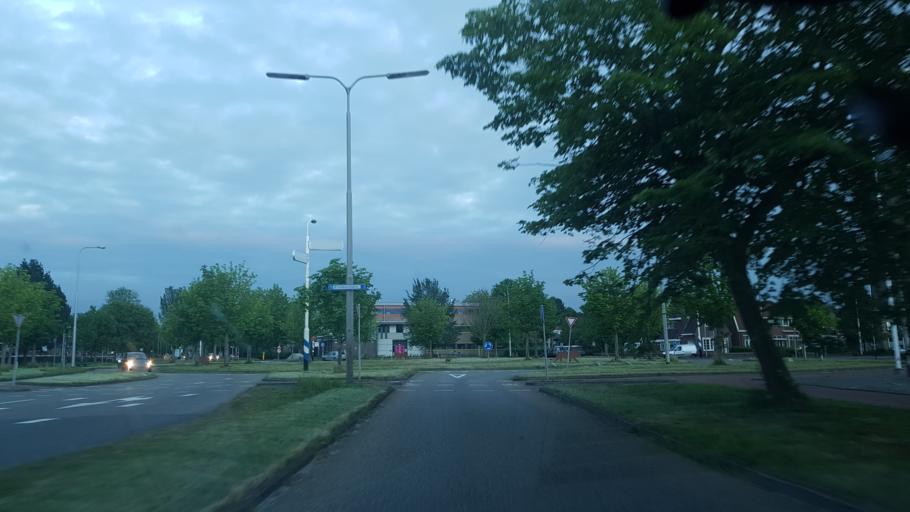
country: NL
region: Friesland
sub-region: Gemeente Leeuwarden
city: Leeuwarden
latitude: 53.2128
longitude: 5.8137
